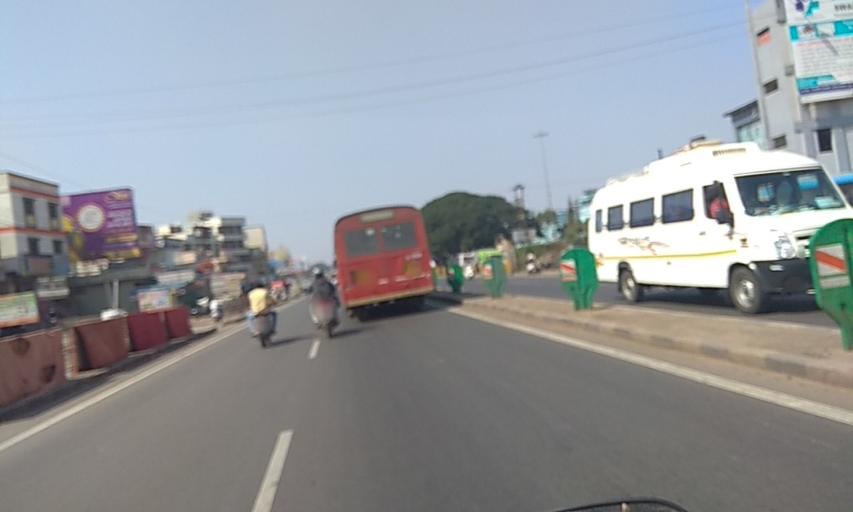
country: IN
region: Maharashtra
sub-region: Pune Division
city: Lohogaon
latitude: 18.4895
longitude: 74.0196
